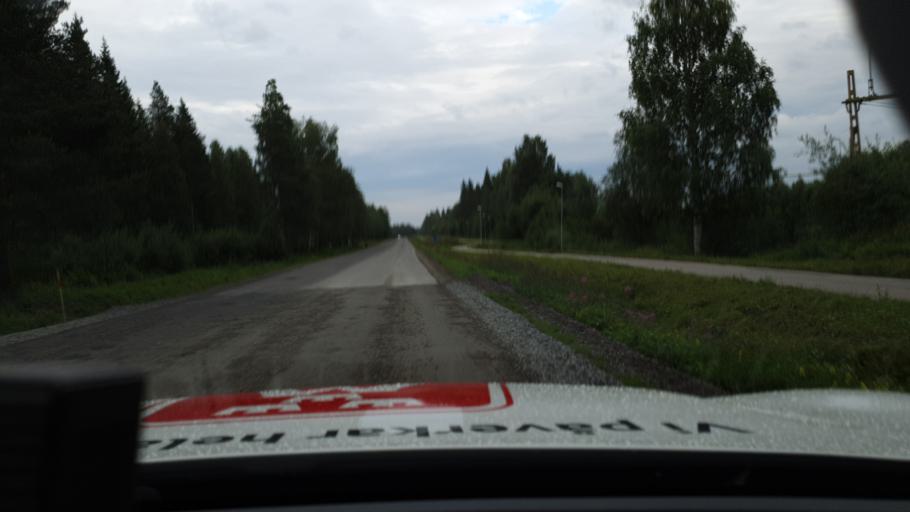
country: SE
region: Norrbotten
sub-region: Bodens Kommun
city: Boden
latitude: 65.8303
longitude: 21.6289
